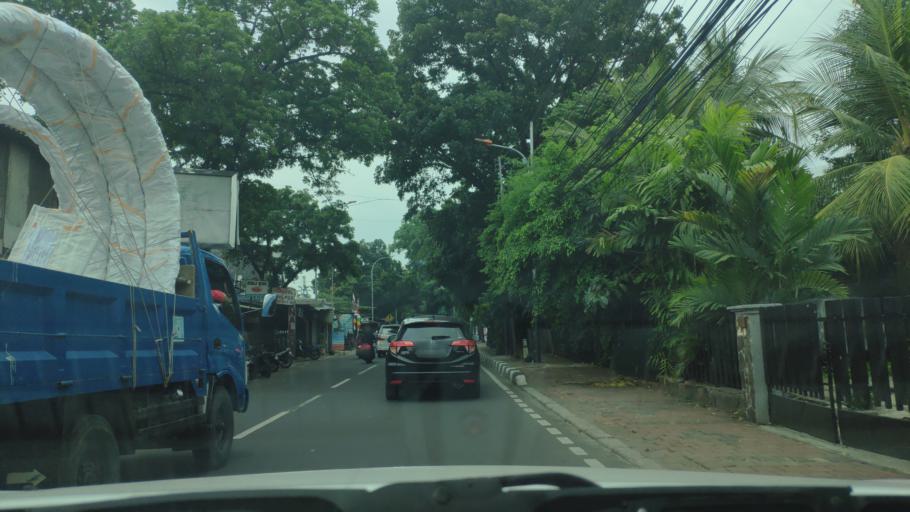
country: ID
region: Jakarta Raya
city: Jakarta
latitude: -6.1899
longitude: 106.7827
